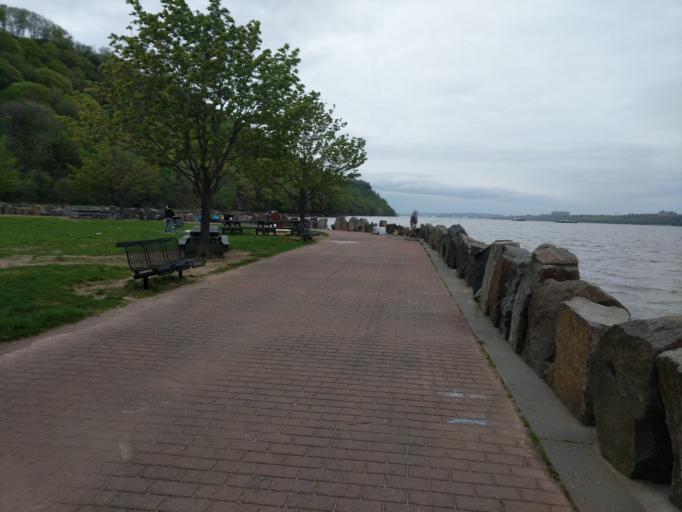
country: US
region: New Jersey
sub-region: Bergen County
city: Fort Lee
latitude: 40.8610
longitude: -73.9539
